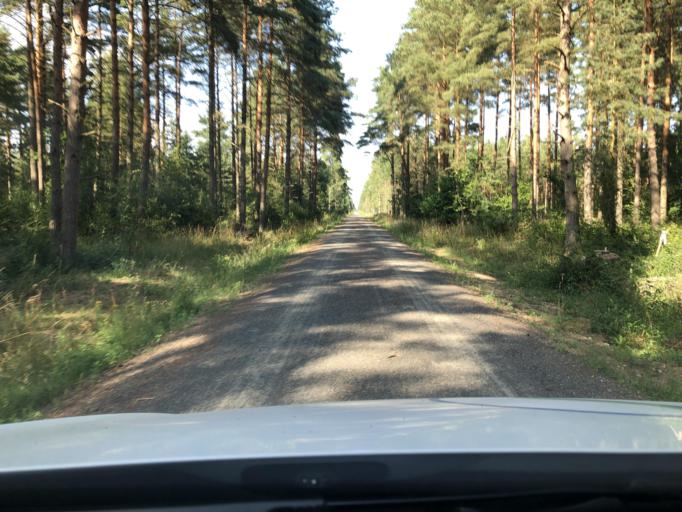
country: SE
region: Skane
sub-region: Kristianstads Kommun
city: Norra Asum
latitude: 55.9275
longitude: 14.1298
